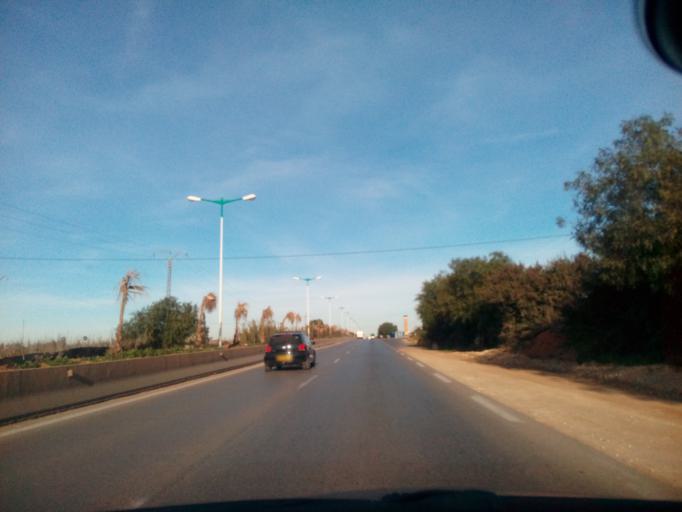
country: DZ
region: Mostaganem
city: Mostaganem
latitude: 35.8573
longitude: 0.1630
